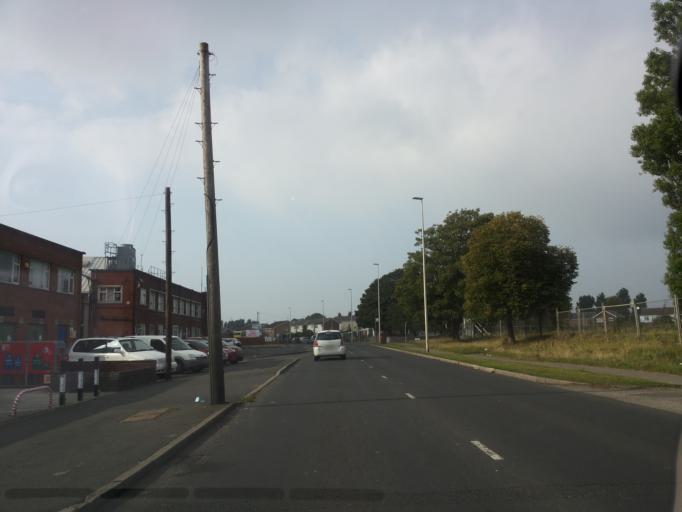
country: GB
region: England
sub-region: Lancashire
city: Great Marton
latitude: 53.7992
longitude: -3.0070
